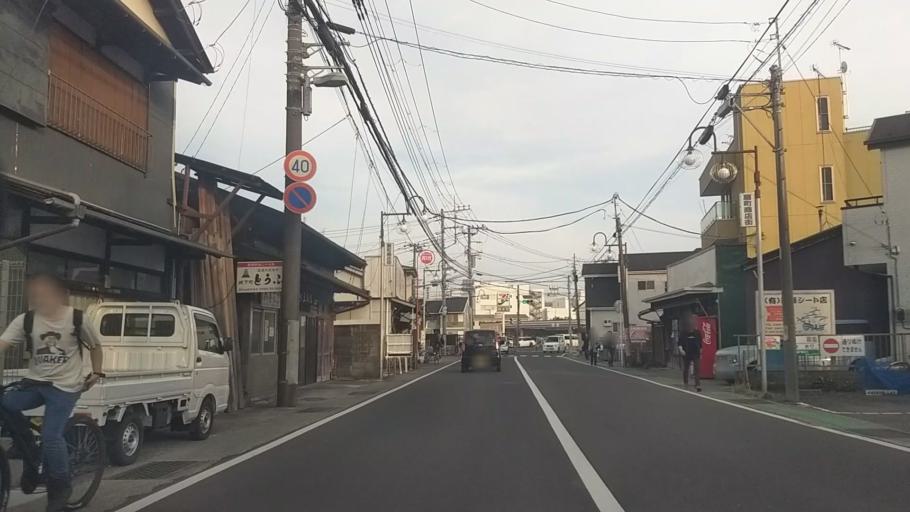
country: JP
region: Kanagawa
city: Odawara
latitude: 35.2701
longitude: 139.1608
